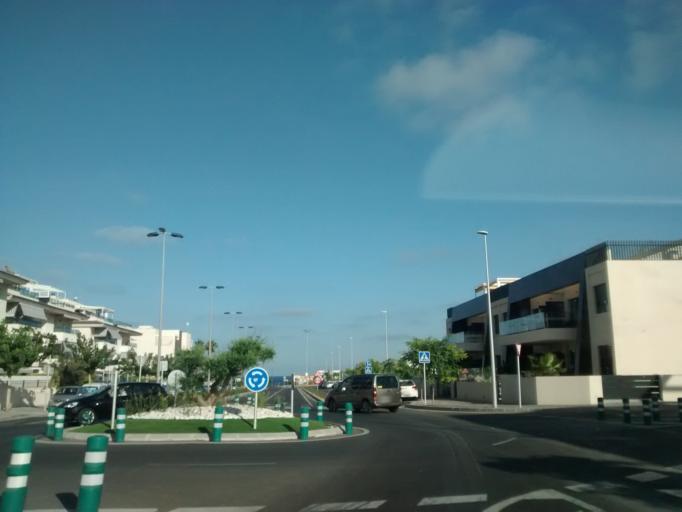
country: ES
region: Valencia
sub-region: Provincia de Alicante
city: Pilar de la Horadada
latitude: 37.8809
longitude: -0.7577
